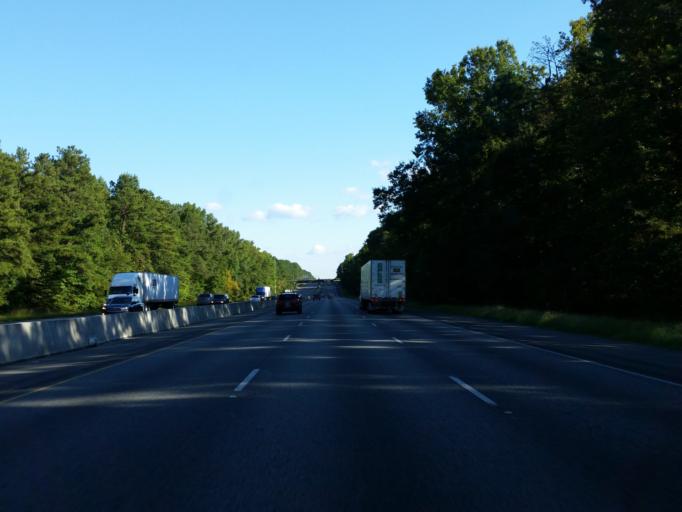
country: US
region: Georgia
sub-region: Bibb County
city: West Point
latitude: 32.9409
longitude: -83.8103
